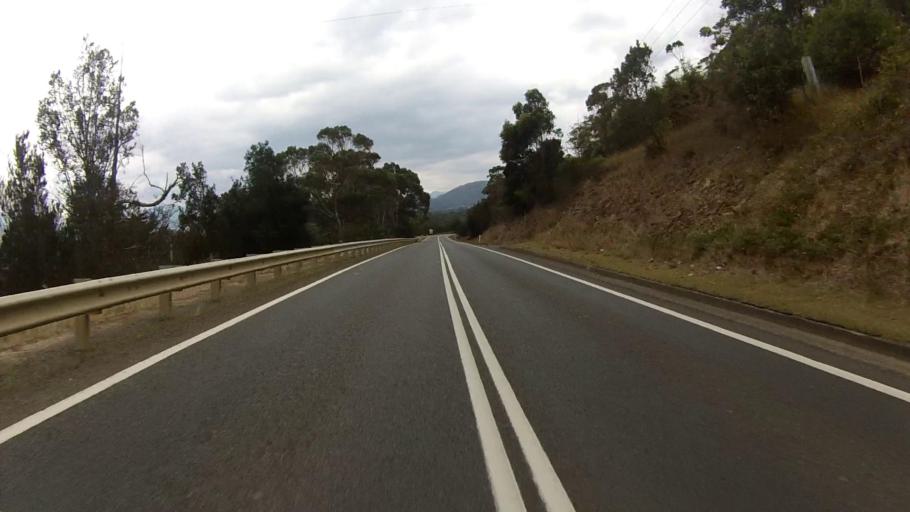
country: AU
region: Tasmania
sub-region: Huon Valley
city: Huonville
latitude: -43.0437
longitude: 147.0518
